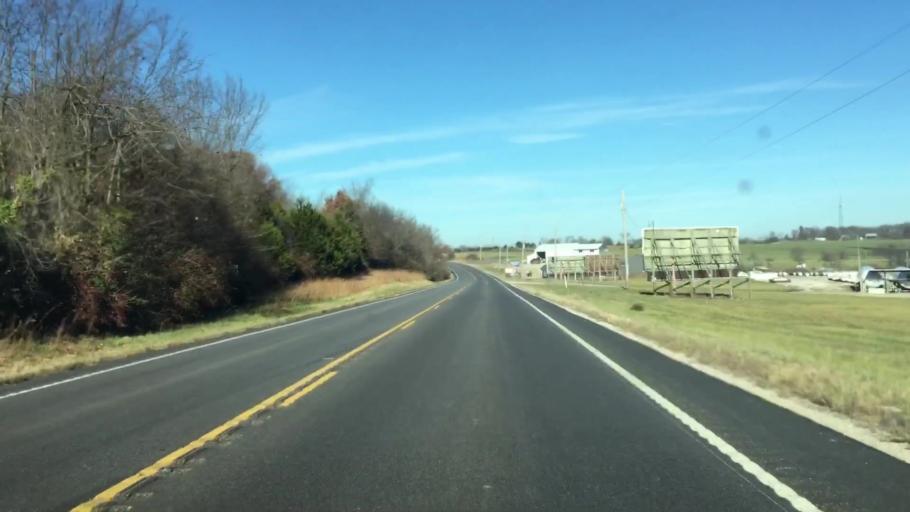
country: US
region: Missouri
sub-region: Miller County
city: Eldon
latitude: 38.3518
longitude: -92.5953
